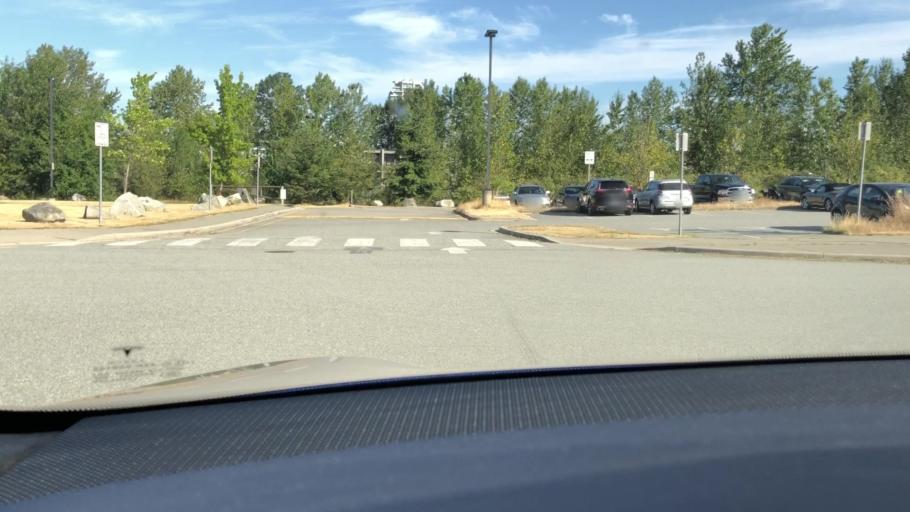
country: CA
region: British Columbia
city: New Westminster
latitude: 49.2089
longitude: -122.9512
